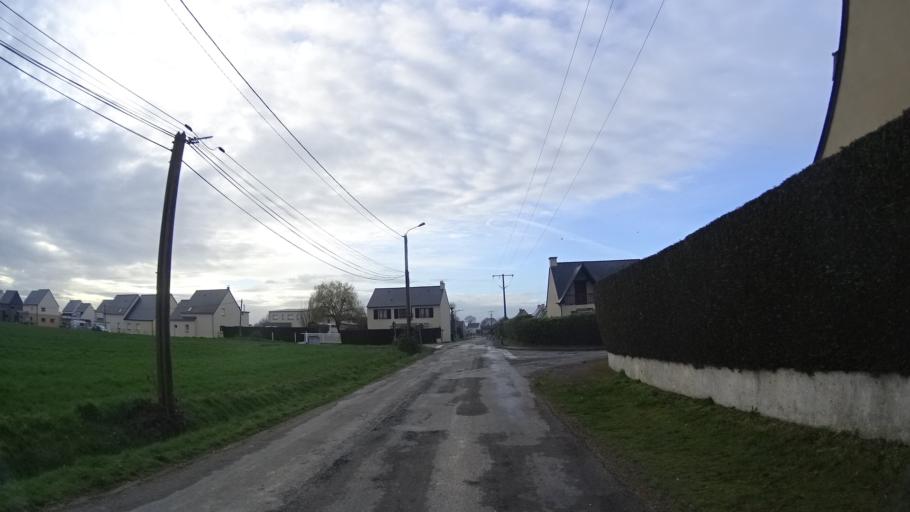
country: FR
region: Brittany
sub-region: Departement d'Ille-et-Vilaine
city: Romille
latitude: 48.2234
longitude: -1.8926
